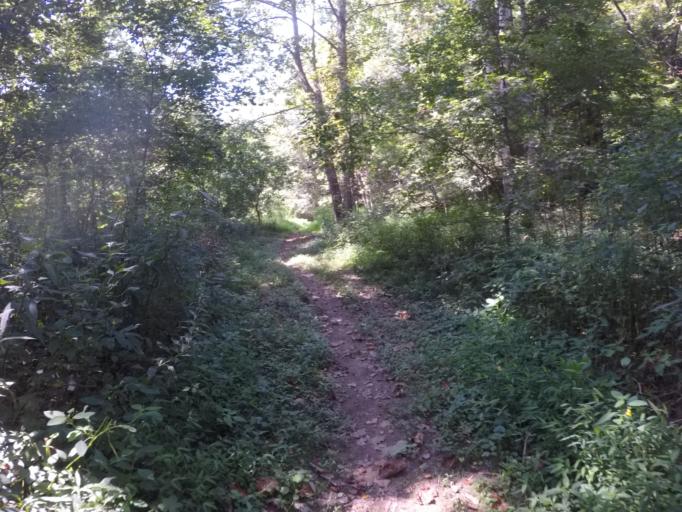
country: US
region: Ohio
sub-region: Lawrence County
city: Ironton
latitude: 38.6306
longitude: -82.6078
